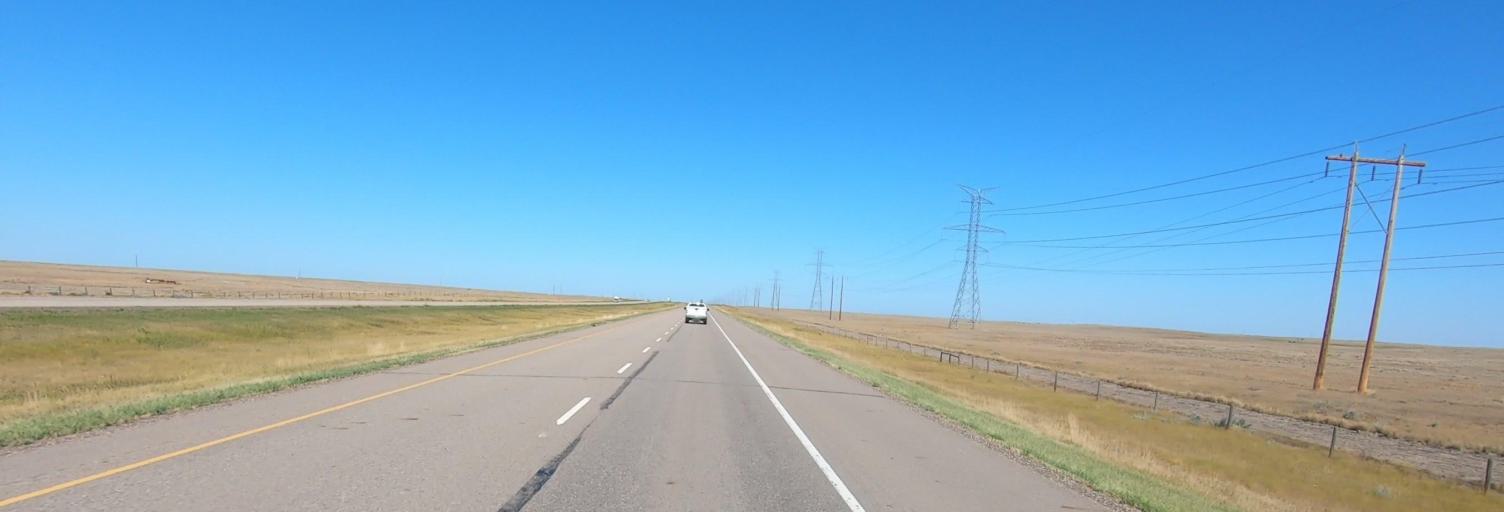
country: CA
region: Alberta
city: Brooks
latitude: 50.3860
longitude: -111.4623
